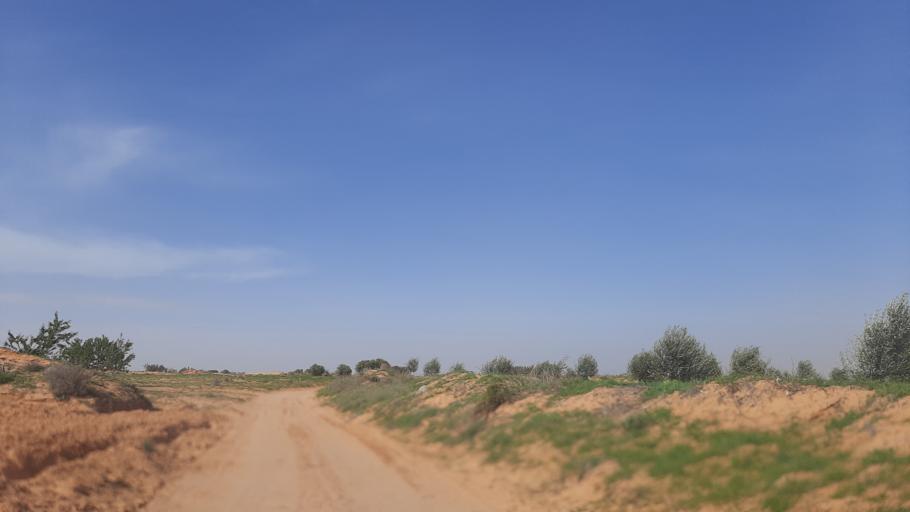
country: TN
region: Madanin
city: Zarzis
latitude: 33.4351
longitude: 10.8087
